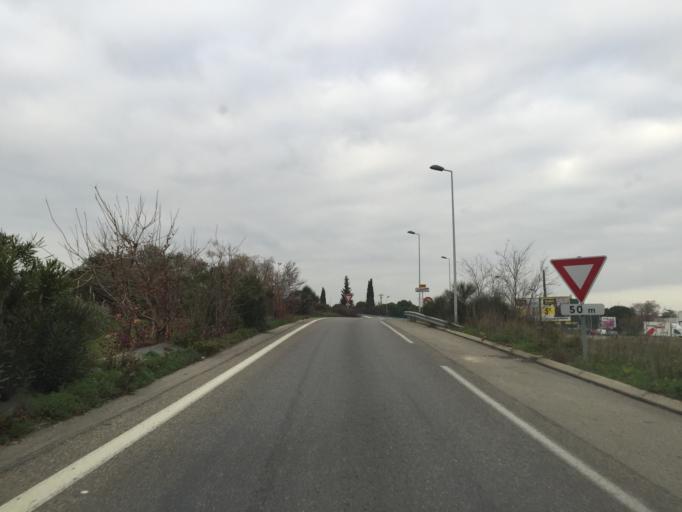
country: FR
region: Provence-Alpes-Cote d'Azur
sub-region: Departement du Vaucluse
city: Sorgues
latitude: 44.0172
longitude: 4.8695
